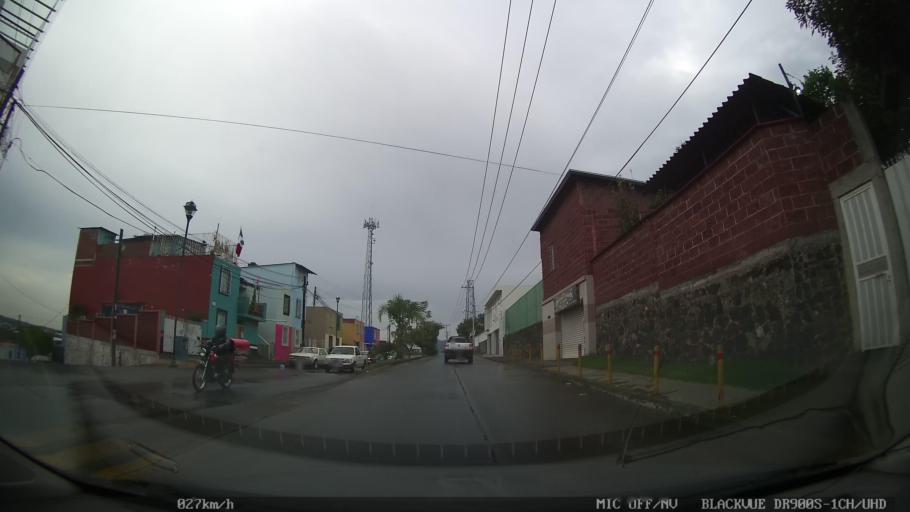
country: MX
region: Michoacan
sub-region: Uruapan
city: Santa Rosa (Santa Barbara)
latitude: 19.3881
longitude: -102.0501
